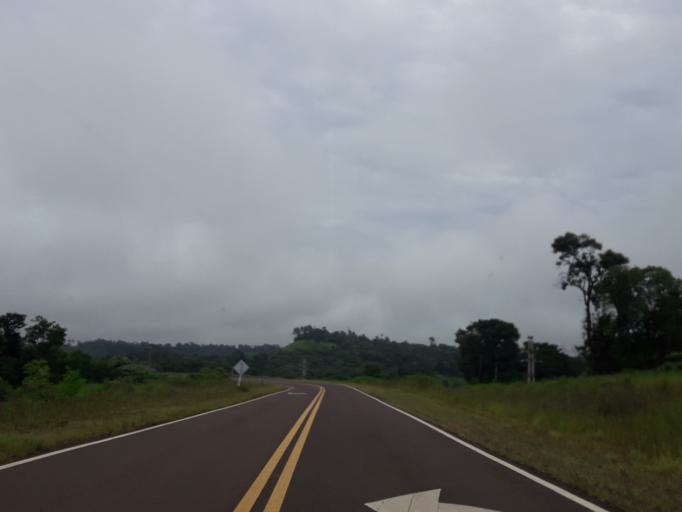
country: AR
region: Misiones
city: Bernardo de Irigoyen
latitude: -26.3924
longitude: -53.8049
